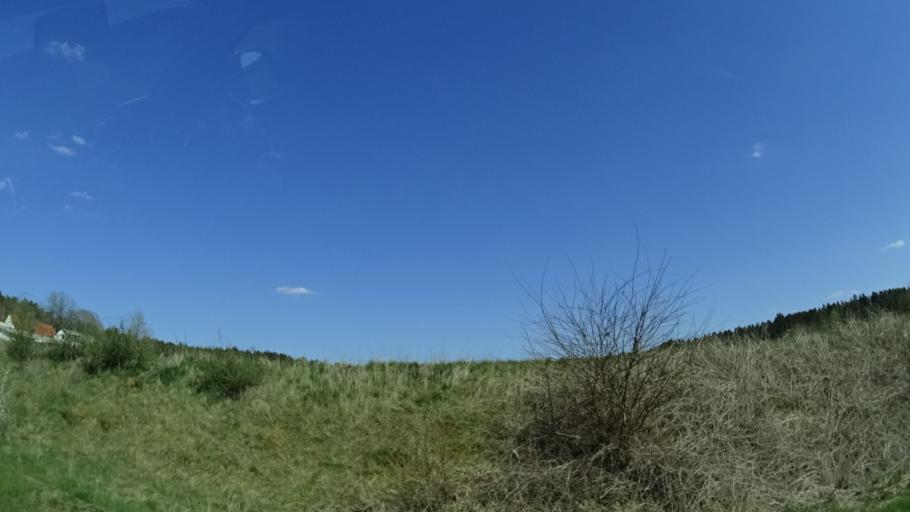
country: DE
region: Bavaria
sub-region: Upper Palatinate
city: Illschwang
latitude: 49.4980
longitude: 11.6544
